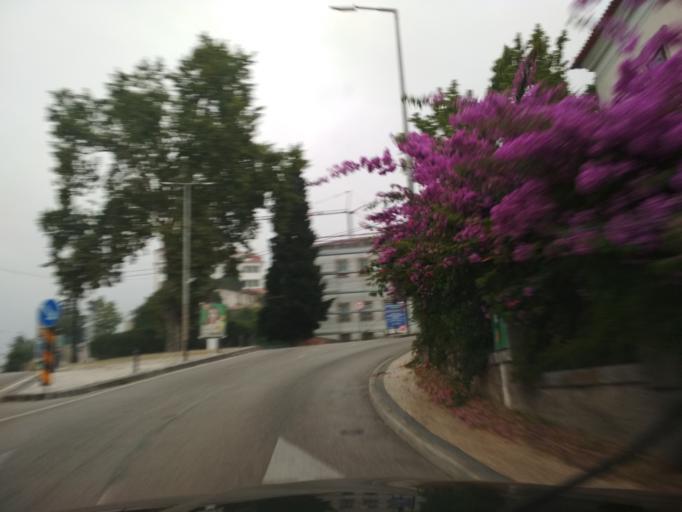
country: PT
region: Coimbra
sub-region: Coimbra
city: Coimbra
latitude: 40.1993
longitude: -8.4212
